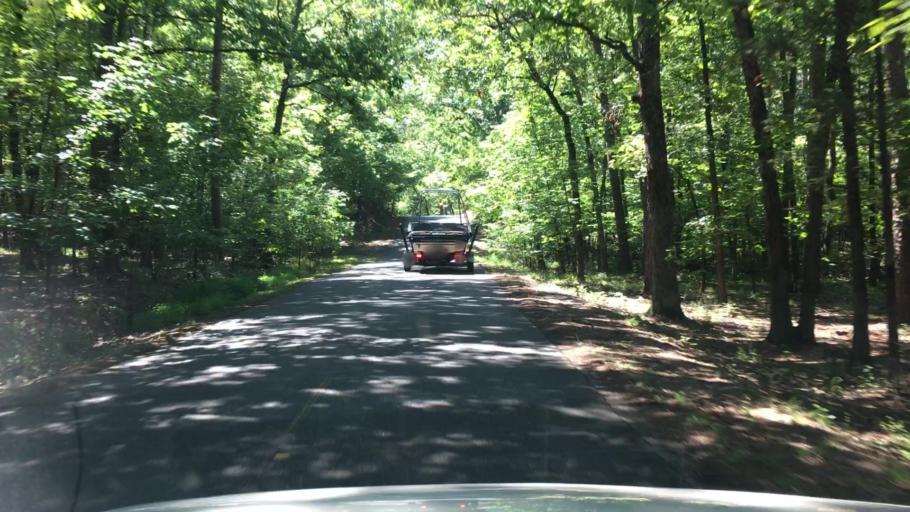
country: US
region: Arkansas
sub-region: Garland County
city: Piney
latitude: 34.5421
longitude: -93.3547
